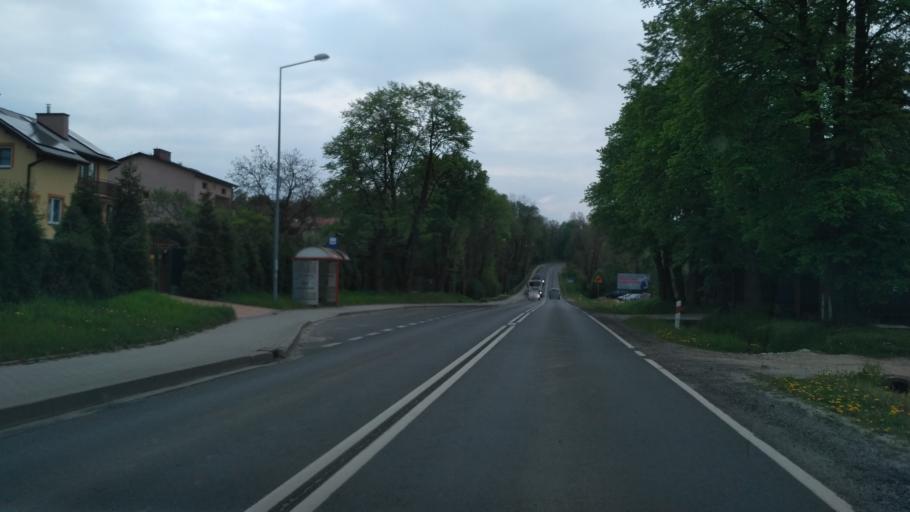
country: PL
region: Lesser Poland Voivodeship
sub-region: Powiat tarnowski
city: Tarnowiec
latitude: 49.9765
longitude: 20.9889
